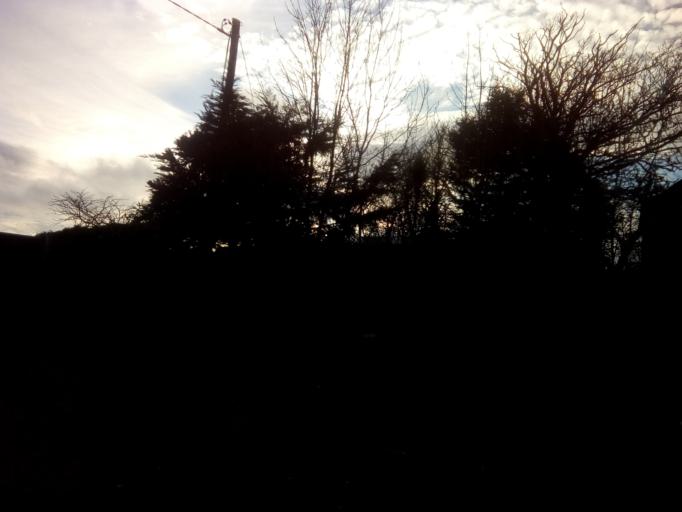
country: IE
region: Leinster
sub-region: Fingal County
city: Skerries
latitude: 53.5687
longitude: -6.1246
